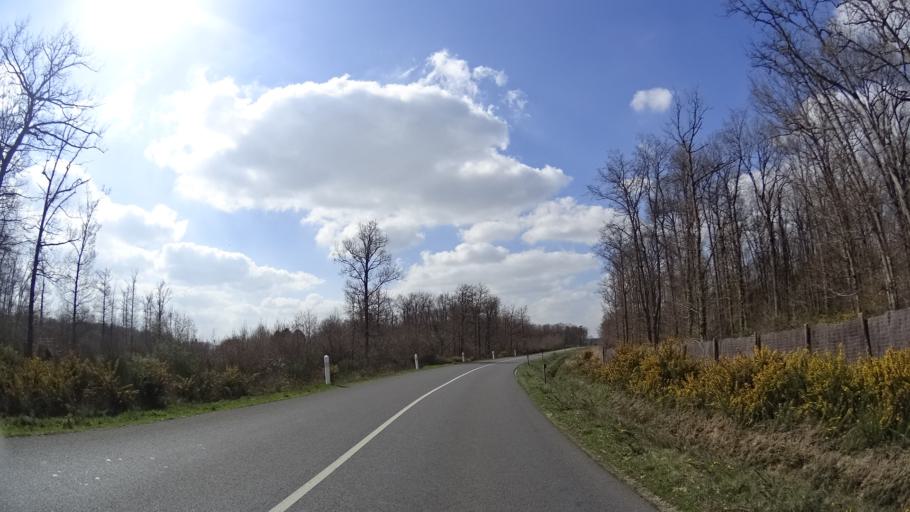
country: FR
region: Pays de la Loire
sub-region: Departement de Maine-et-Loire
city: Breze
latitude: 47.0897
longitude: -0.0035
